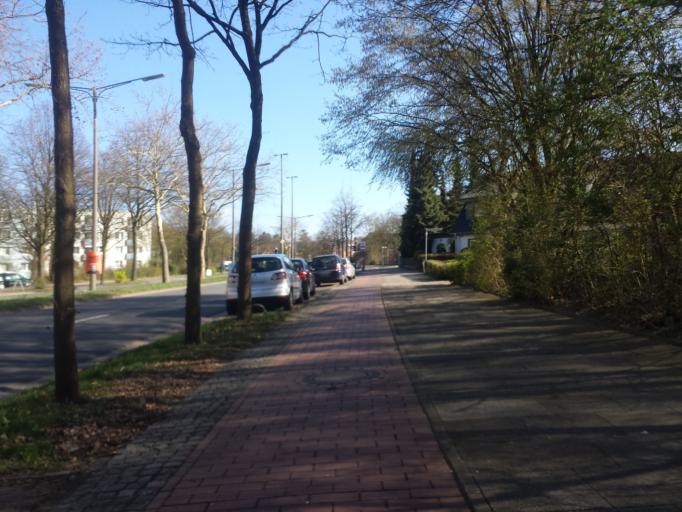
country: DE
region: Lower Saxony
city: Lilienthal
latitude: 53.0715
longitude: 8.9293
